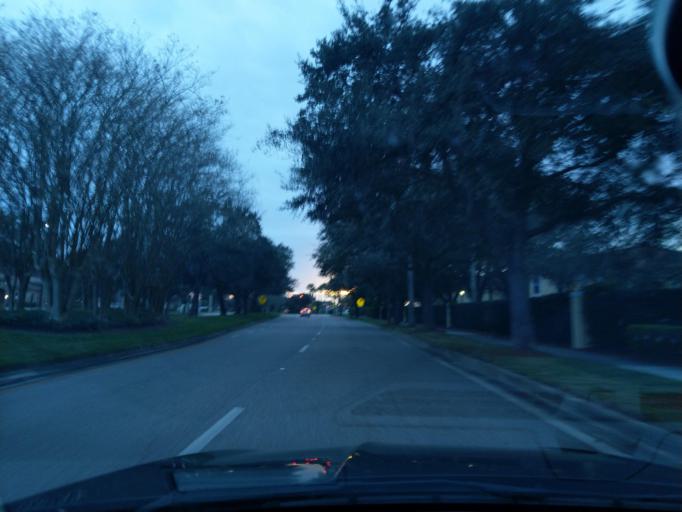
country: US
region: Florida
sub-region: Orange County
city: Hunters Creek
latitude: 28.3629
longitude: -81.4278
